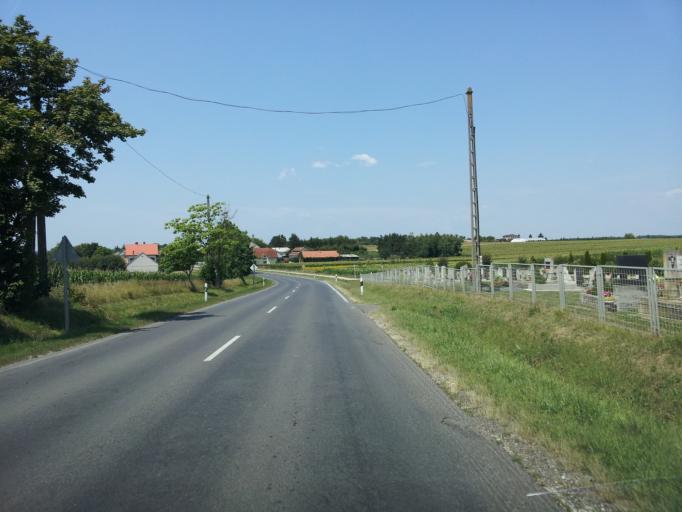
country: HU
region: Zala
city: Zalaegerszeg
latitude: 46.8752
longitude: 16.7629
